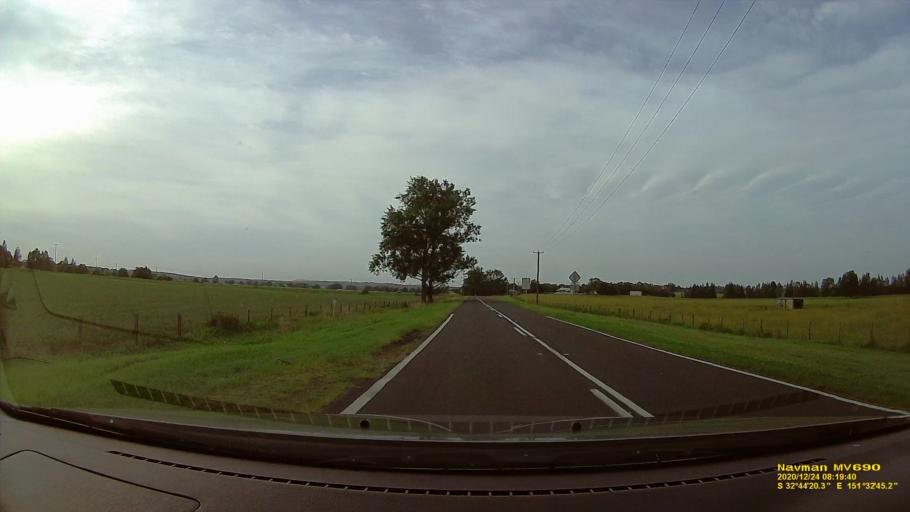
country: AU
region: New South Wales
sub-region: Maitland Municipality
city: Maitland
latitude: -32.7389
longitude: 151.5459
